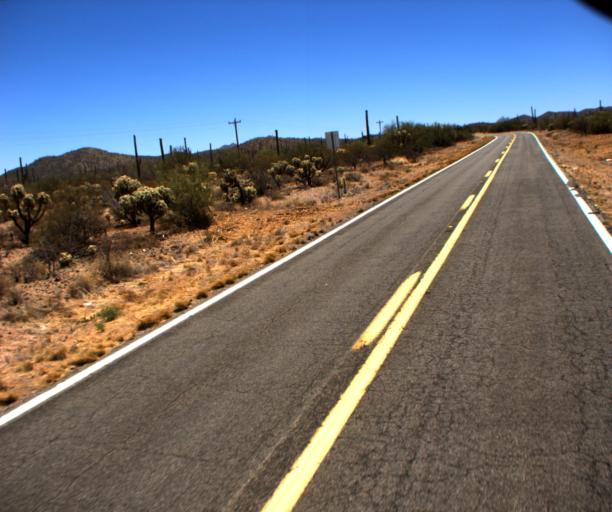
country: US
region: Arizona
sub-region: Pima County
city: Sells
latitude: 32.1765
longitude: -112.2394
